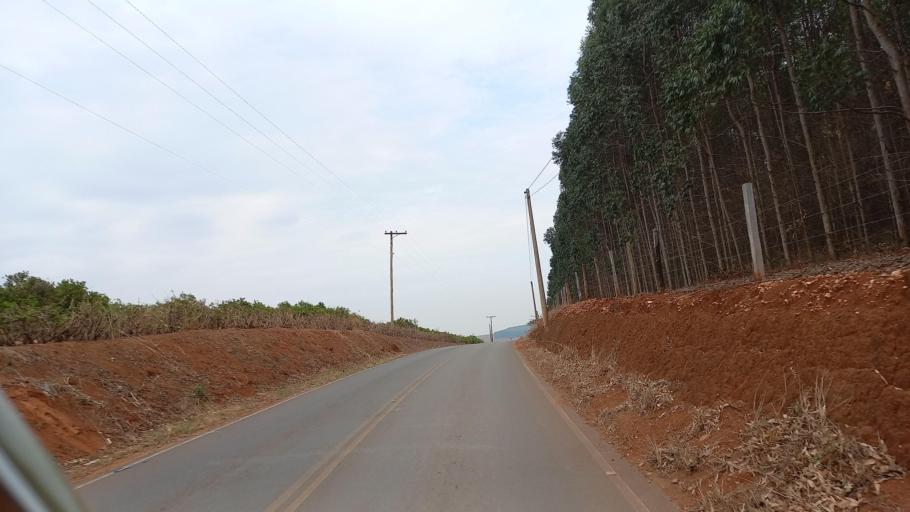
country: BR
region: Sao Paulo
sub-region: Moji-Guacu
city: Mogi-Gaucu
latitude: -22.3297
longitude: -46.8693
